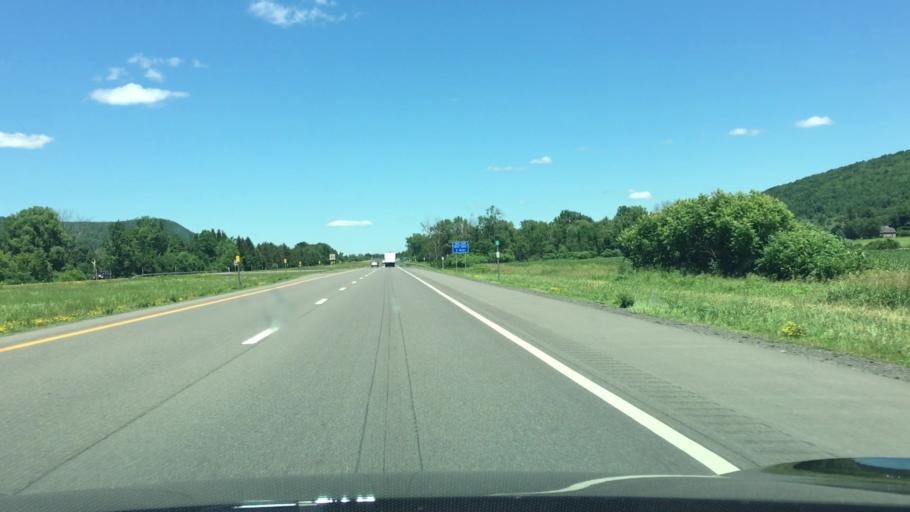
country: US
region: New York
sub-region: Cortland County
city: Homer
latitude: 42.6807
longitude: -76.1639
